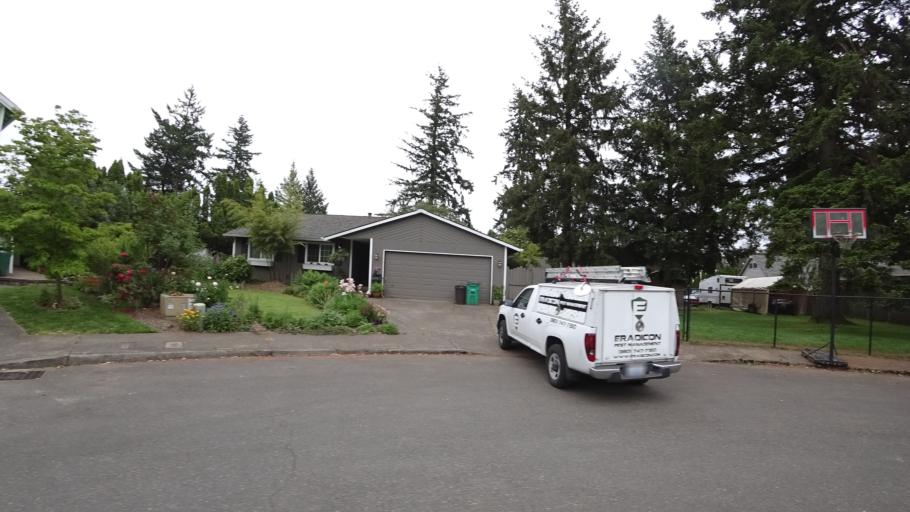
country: US
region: Oregon
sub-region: Multnomah County
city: Lents
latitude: 45.5108
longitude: -122.5311
